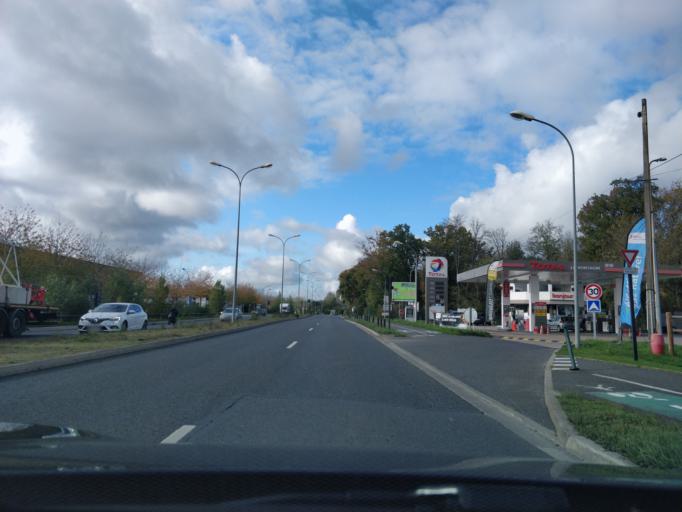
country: FR
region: Ile-de-France
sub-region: Departement de l'Essonne
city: Arpajon
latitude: 48.5995
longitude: 2.2404
